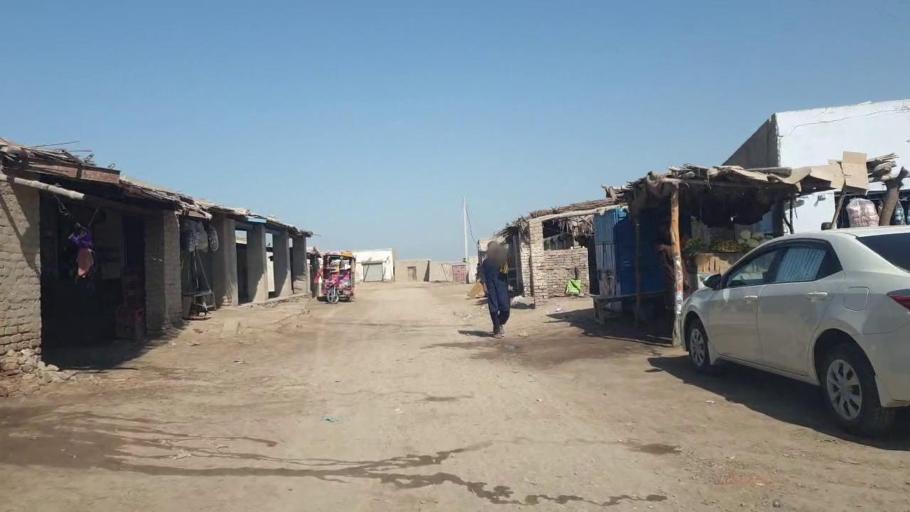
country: PK
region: Sindh
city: Umarkot
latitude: 25.2891
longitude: 69.6523
